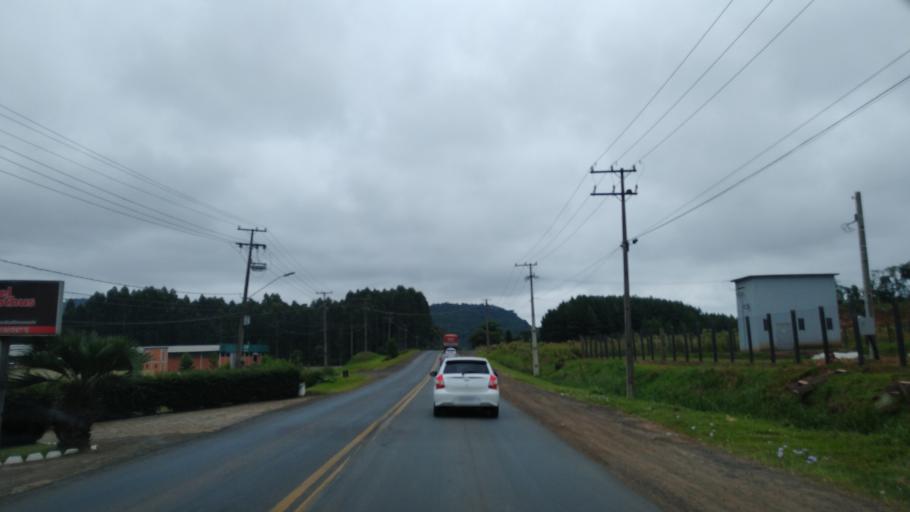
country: BR
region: Parana
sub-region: Uniao Da Vitoria
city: Uniao da Vitoria
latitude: -26.2419
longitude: -51.1234
